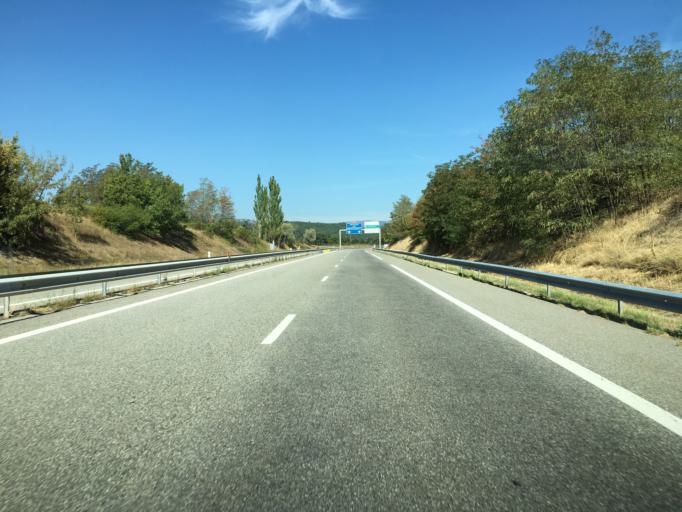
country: FR
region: Provence-Alpes-Cote d'Azur
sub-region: Departement des Alpes-de-Haute-Provence
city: Sisteron
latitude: 44.2160
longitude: 5.9247
